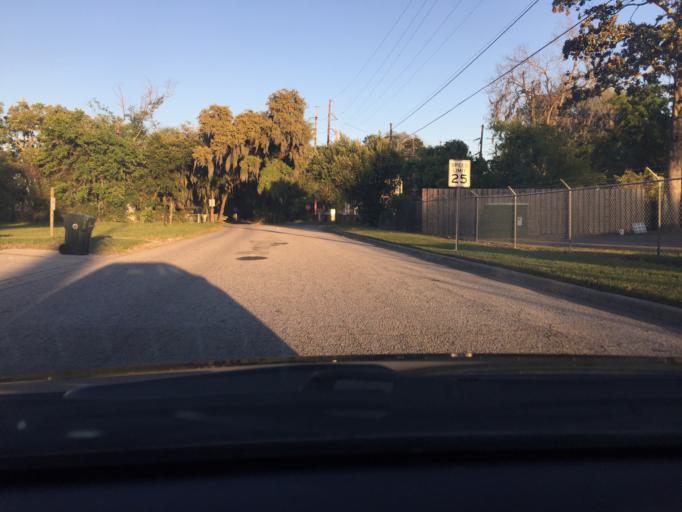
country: US
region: Georgia
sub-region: Chatham County
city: Montgomery
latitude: 31.9969
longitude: -81.1227
